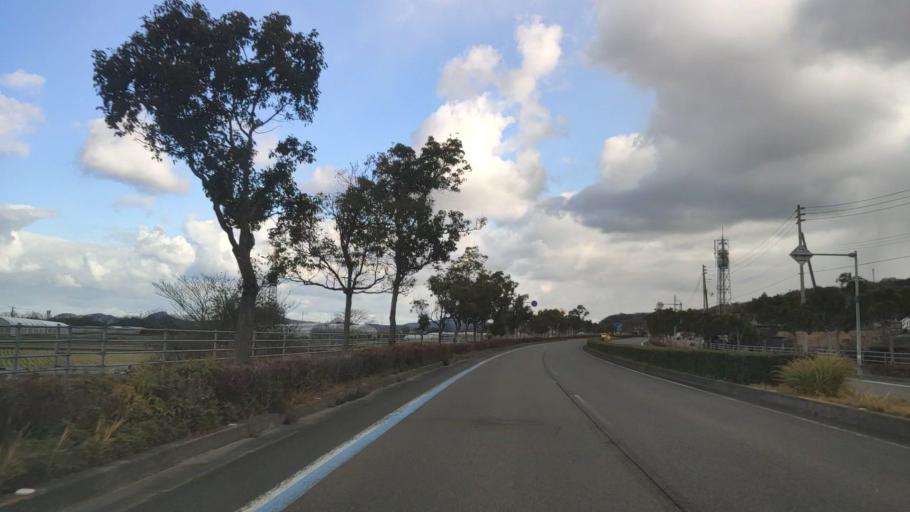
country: JP
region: Ehime
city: Hojo
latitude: 33.9334
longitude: 132.7674
